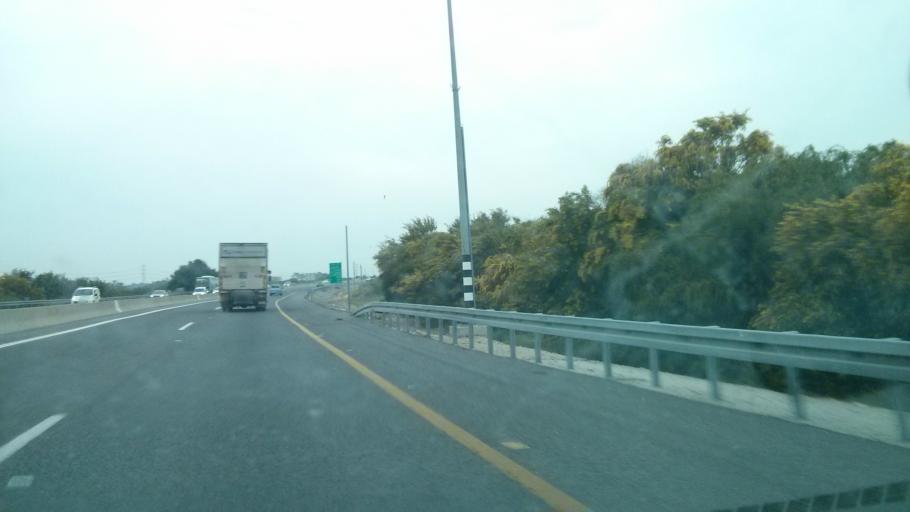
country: IL
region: Haifa
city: Qesarya
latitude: 32.4973
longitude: 34.9173
